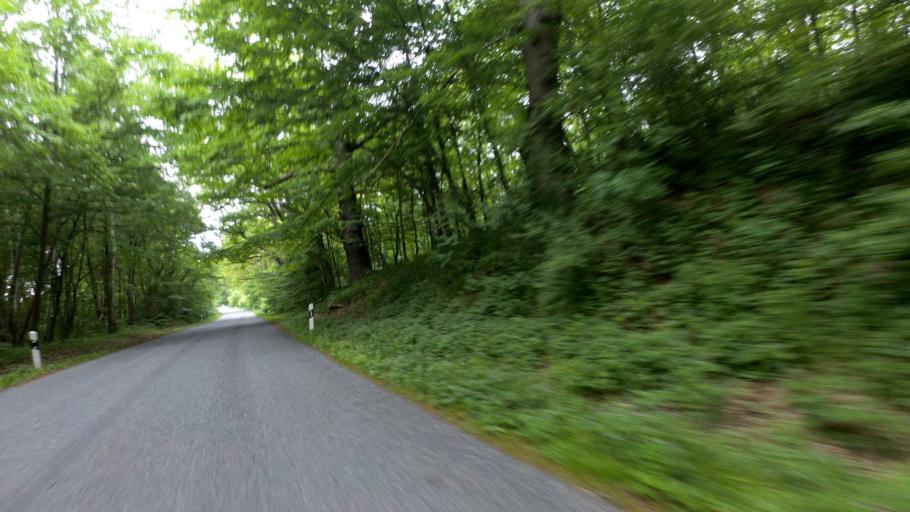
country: DE
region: Mecklenburg-Vorpommern
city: Mollenhagen
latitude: 53.6155
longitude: 12.9053
